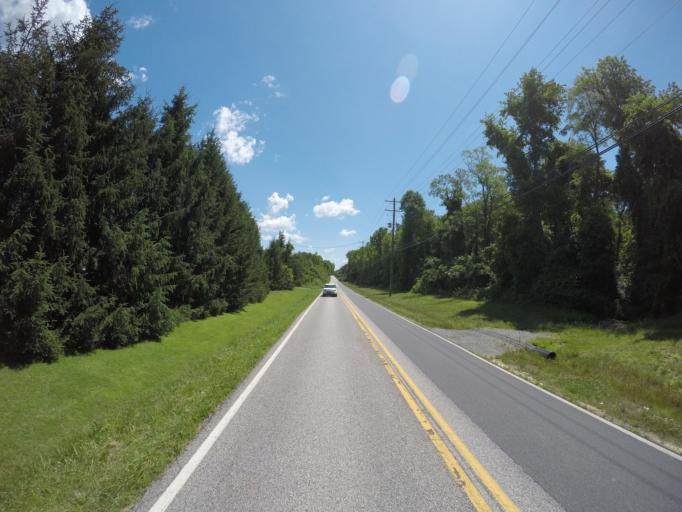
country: US
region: Delaware
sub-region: New Castle County
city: Glasgow
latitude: 39.5724
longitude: -75.7159
